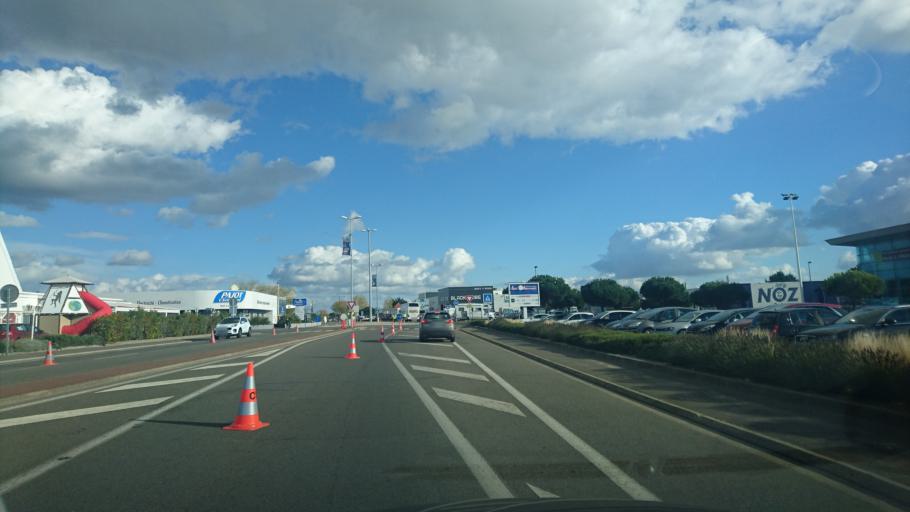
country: FR
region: Pays de la Loire
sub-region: Departement de la Vendee
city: Les Sables-d'Olonne
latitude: 46.5135
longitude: -1.7809
